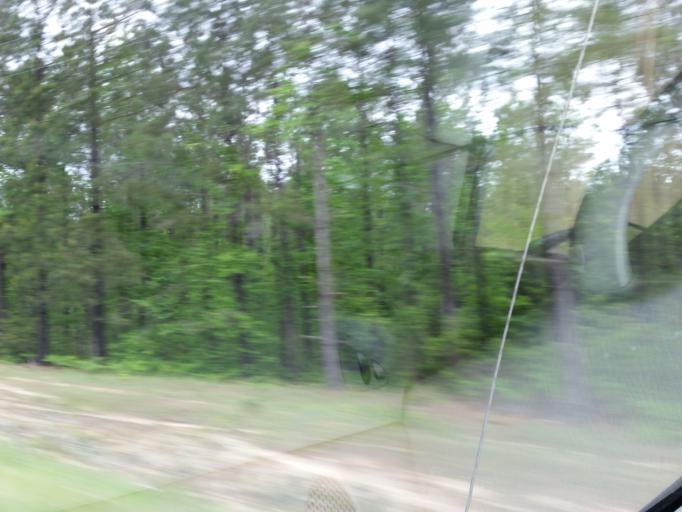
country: US
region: Georgia
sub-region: Crawford County
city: Knoxville
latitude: 32.6857
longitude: -83.9179
